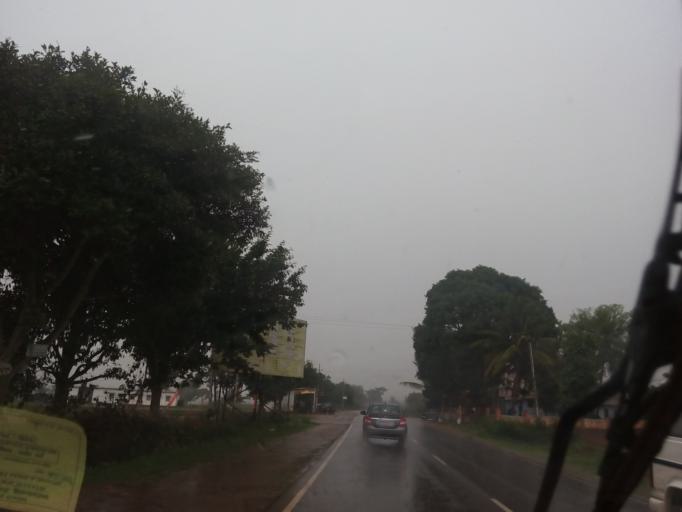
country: IN
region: Karnataka
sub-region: Hassan
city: Belur
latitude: 13.1200
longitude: 75.9999
